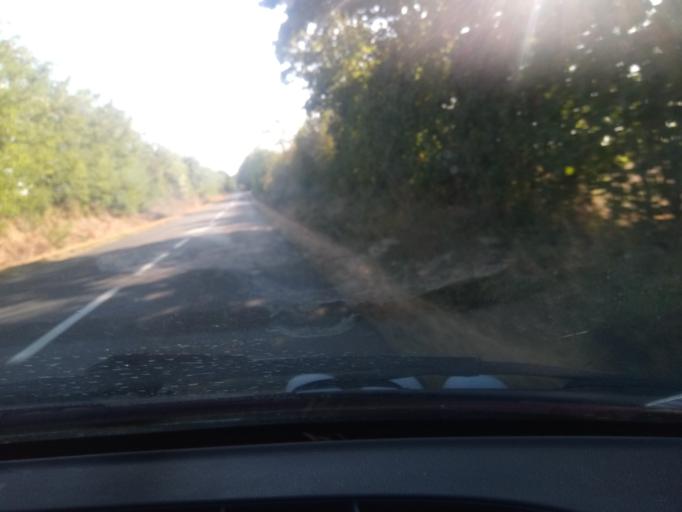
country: FR
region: Poitou-Charentes
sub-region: Departement de la Vienne
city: Lussac-les-Chateaux
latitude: 46.3774
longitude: 0.7101
